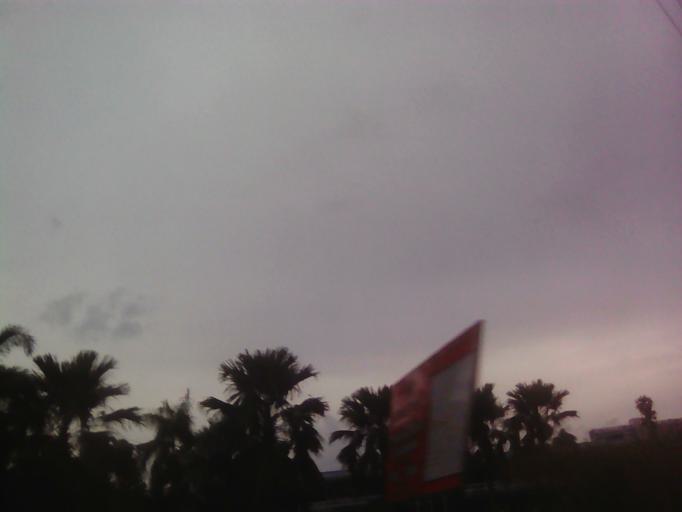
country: MY
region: Penang
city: Perai
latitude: 5.4002
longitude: 100.4019
